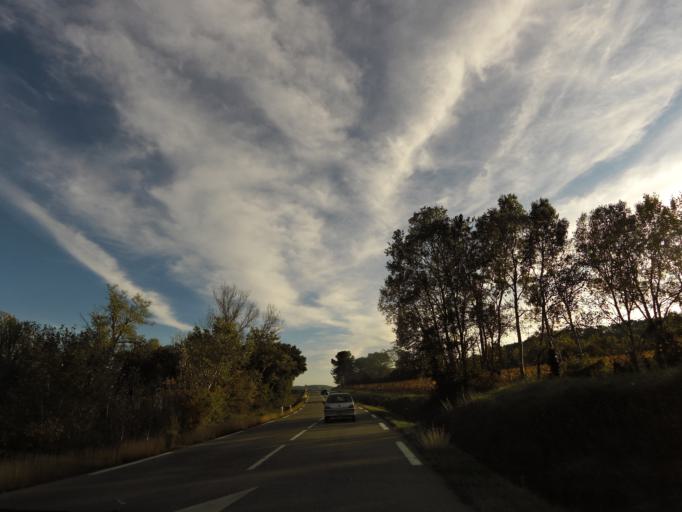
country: FR
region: Languedoc-Roussillon
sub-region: Departement du Gard
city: Ledignan
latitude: 43.9368
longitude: 4.1018
